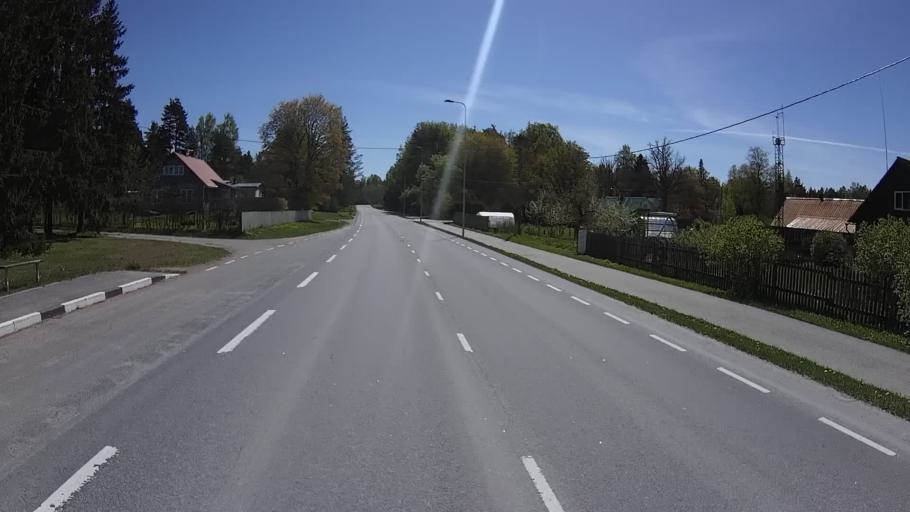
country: EE
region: Harju
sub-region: Raasiku vald
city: Raasiku
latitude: 59.1768
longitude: 25.1695
